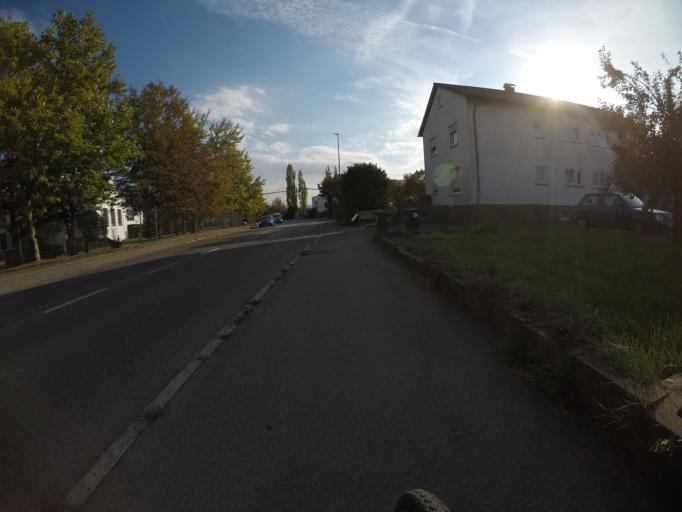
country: DE
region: Baden-Wuerttemberg
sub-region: Tuebingen Region
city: Pliezhausen
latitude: 48.5396
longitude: 9.2017
